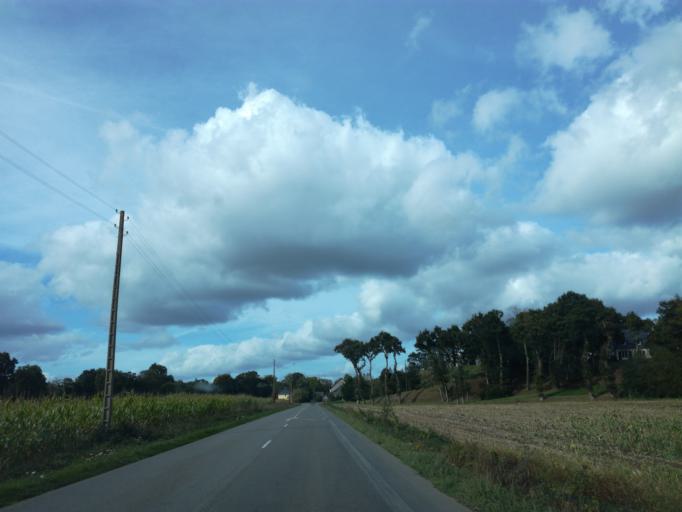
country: FR
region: Brittany
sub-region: Departement du Morbihan
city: Rohan
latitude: 48.0802
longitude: -2.7607
